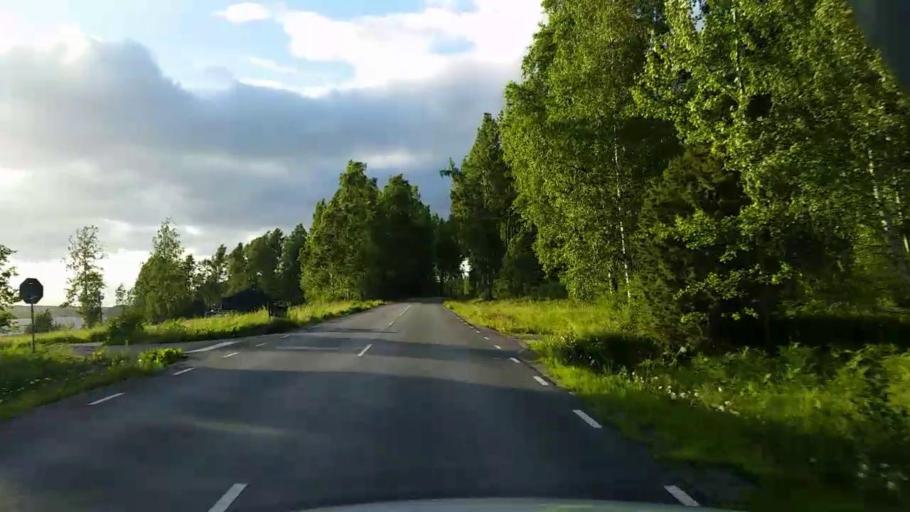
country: SE
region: Vaestmanland
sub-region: Kopings Kommun
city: Kolsva
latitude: 59.7062
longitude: 15.8293
